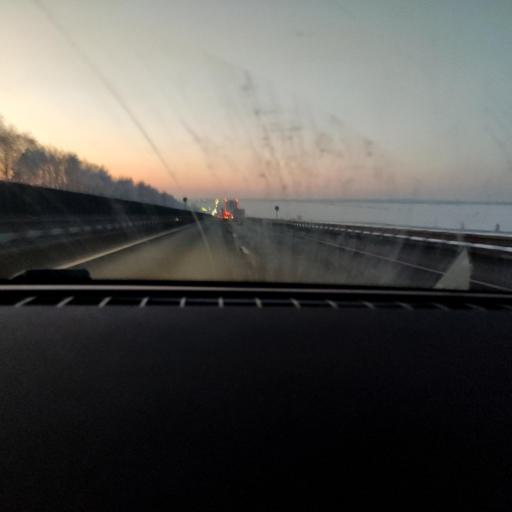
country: RU
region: Samara
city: Mirnyy
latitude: 53.4528
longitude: 50.2388
